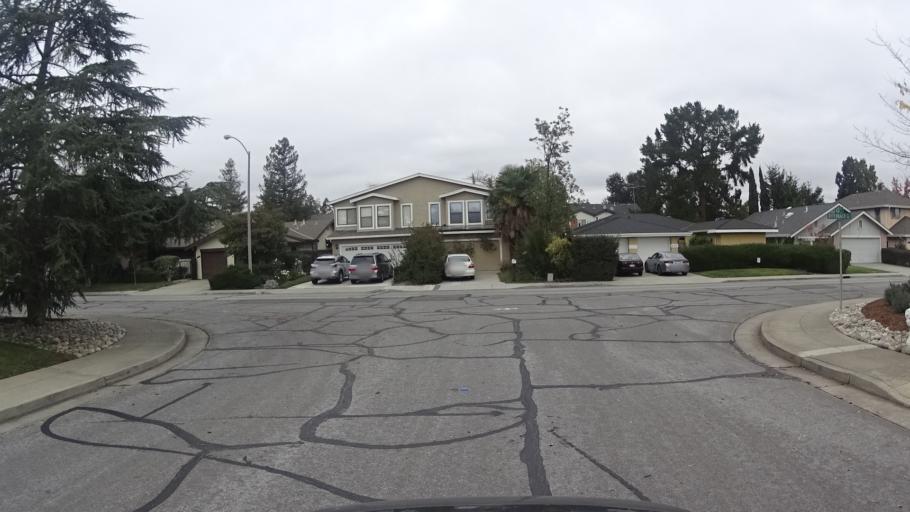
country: US
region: California
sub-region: Santa Clara County
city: Sunnyvale
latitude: 37.3546
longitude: -122.0290
